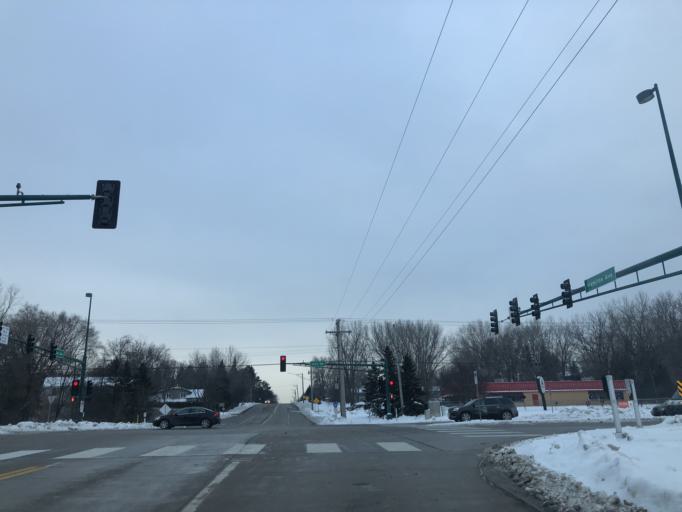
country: US
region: Minnesota
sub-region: Ramsey County
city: Shoreview
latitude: 45.0796
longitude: -93.1576
